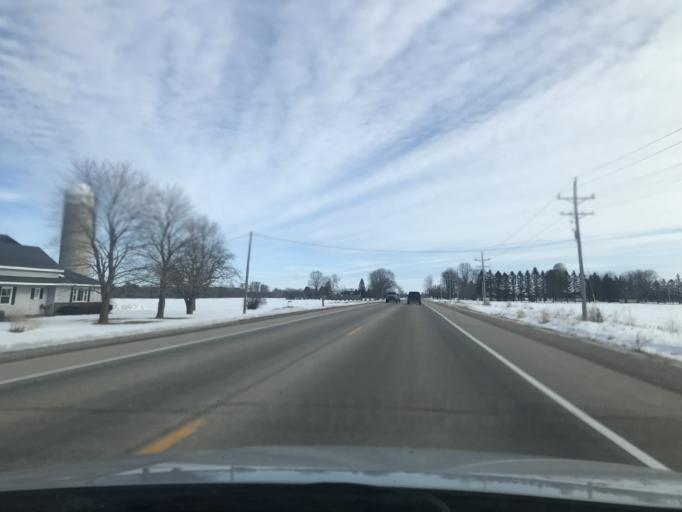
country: US
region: Wisconsin
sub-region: Oconto County
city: Gillett
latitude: 44.8962
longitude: -88.2707
